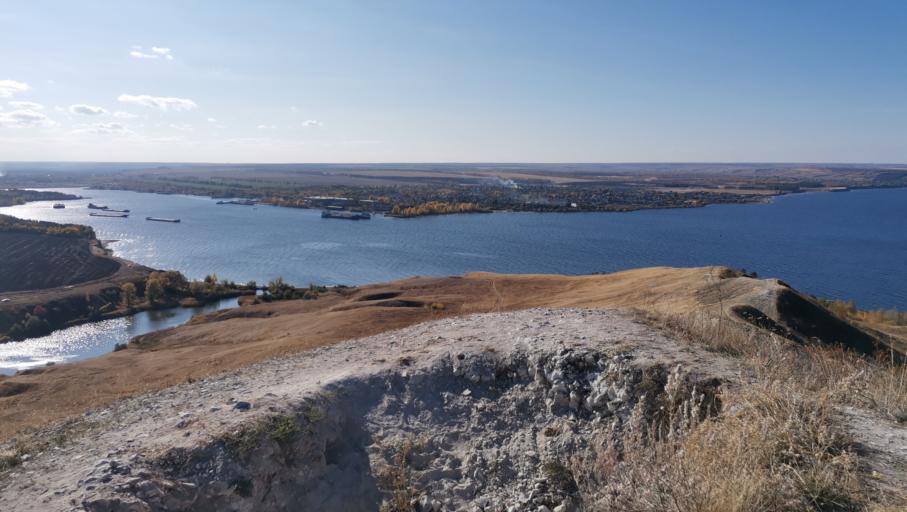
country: RU
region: Ulyanovsk
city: Novoul'yanovsk
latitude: 54.1131
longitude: 48.5688
